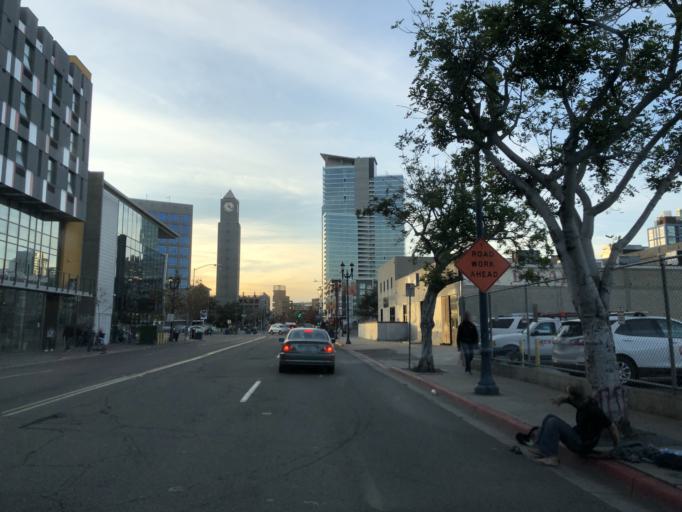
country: US
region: California
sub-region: San Diego County
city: San Diego
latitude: 32.7063
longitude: -117.1509
